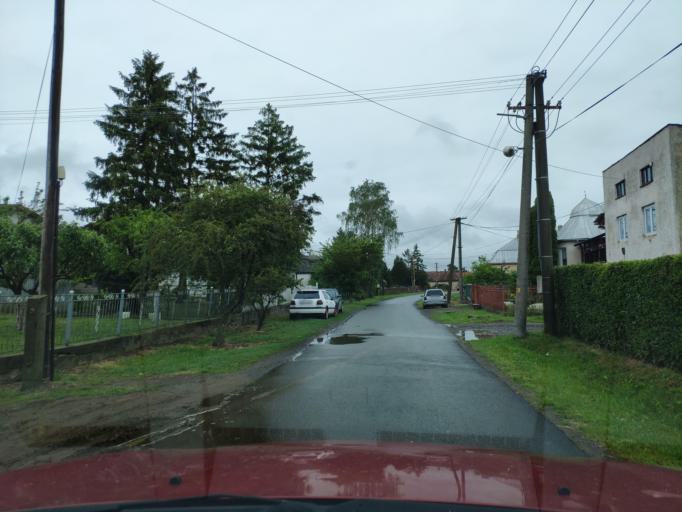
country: SK
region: Kosicky
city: Cierna nad Tisou
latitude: 48.4065
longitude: 22.0613
